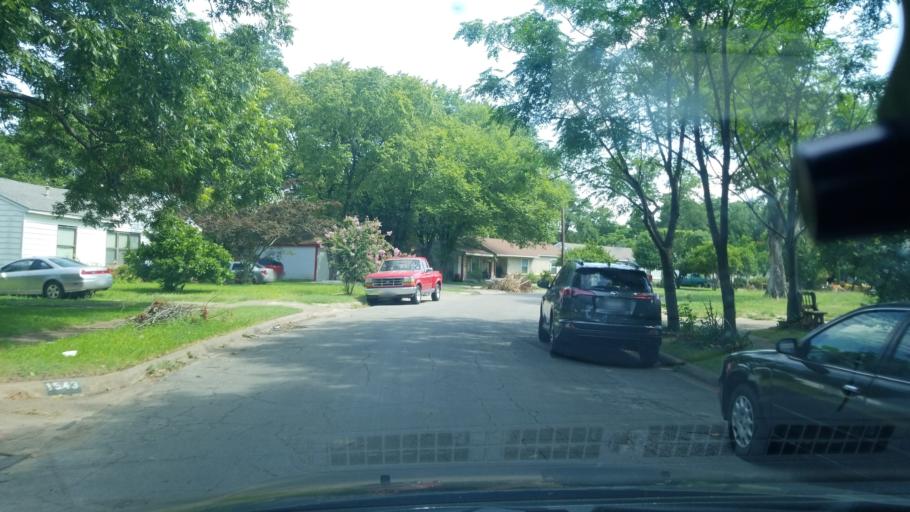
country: US
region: Texas
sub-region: Dallas County
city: Balch Springs
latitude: 32.7391
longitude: -96.6927
